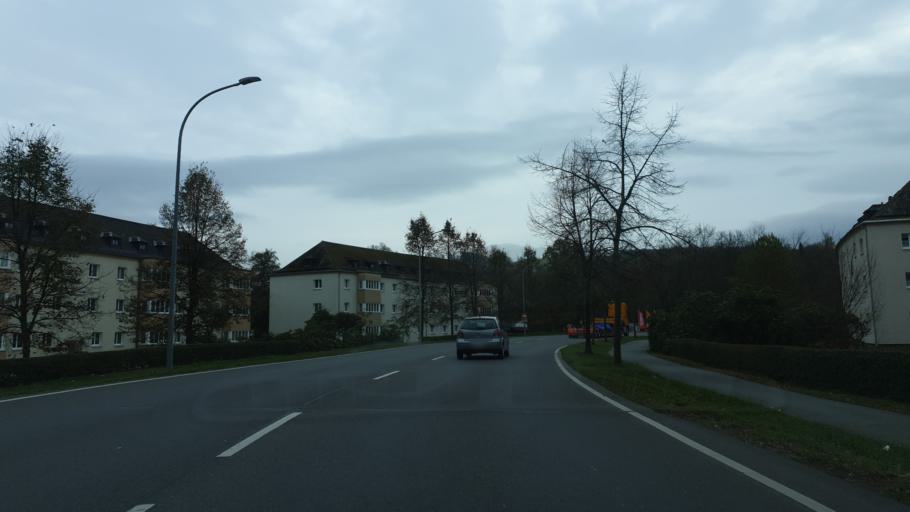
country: DE
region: Saxony
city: Schwarzenberg
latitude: 50.5450
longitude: 12.7927
